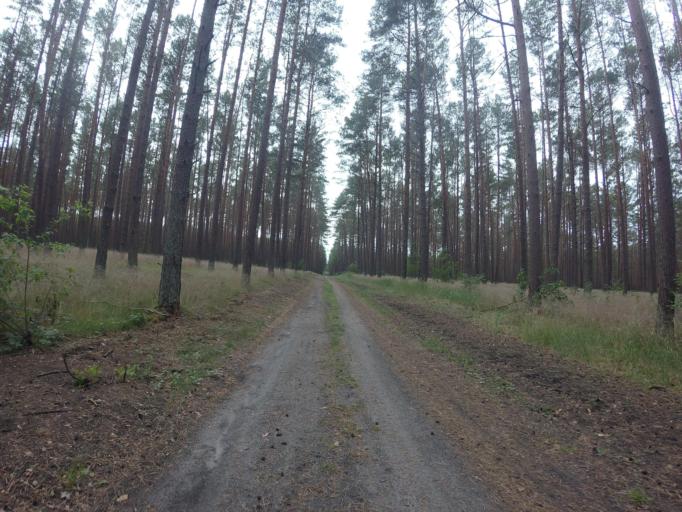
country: PL
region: West Pomeranian Voivodeship
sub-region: Powiat choszczenski
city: Bierzwnik
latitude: 53.1132
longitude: 15.6888
